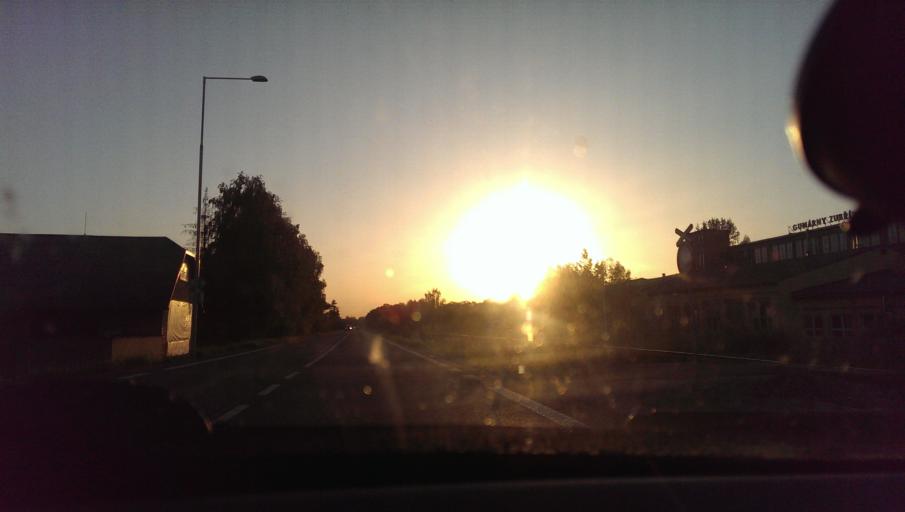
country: CZ
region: Zlin
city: Zubri
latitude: 49.4613
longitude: 18.0899
